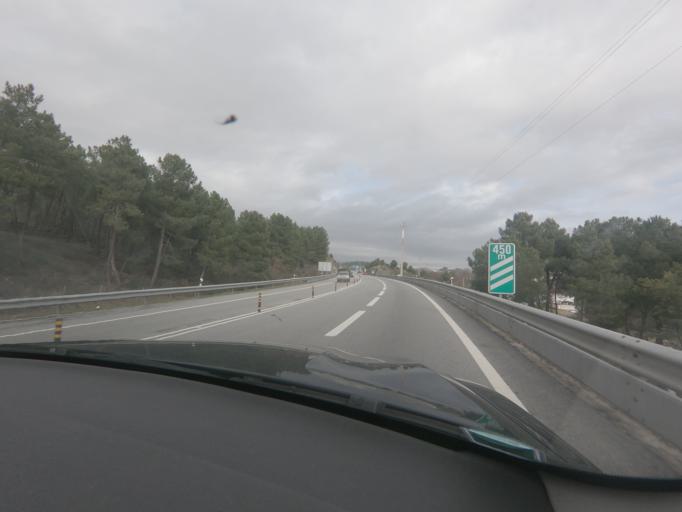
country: PT
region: Vila Real
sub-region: Vila Real
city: Vila Real
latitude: 41.3173
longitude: -7.7051
